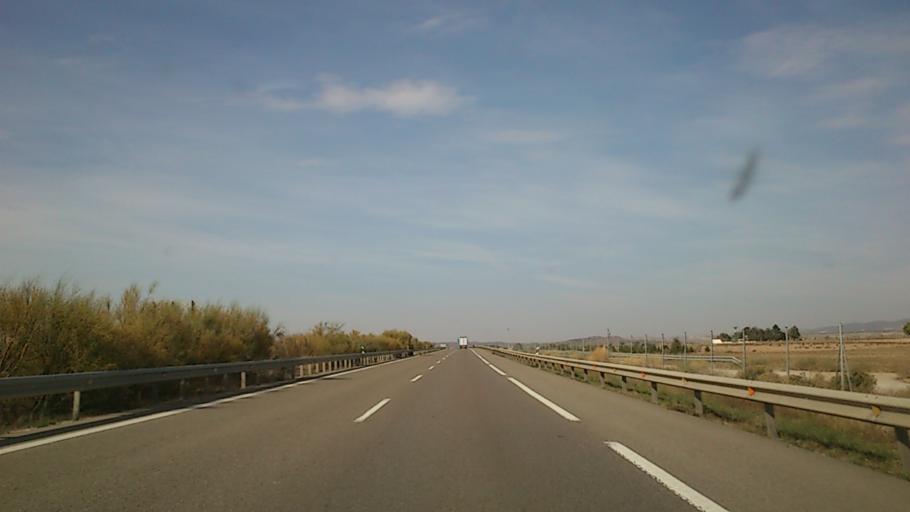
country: ES
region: Aragon
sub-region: Provincia de Teruel
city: Fuentes Claras
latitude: 40.8600
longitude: -1.3088
